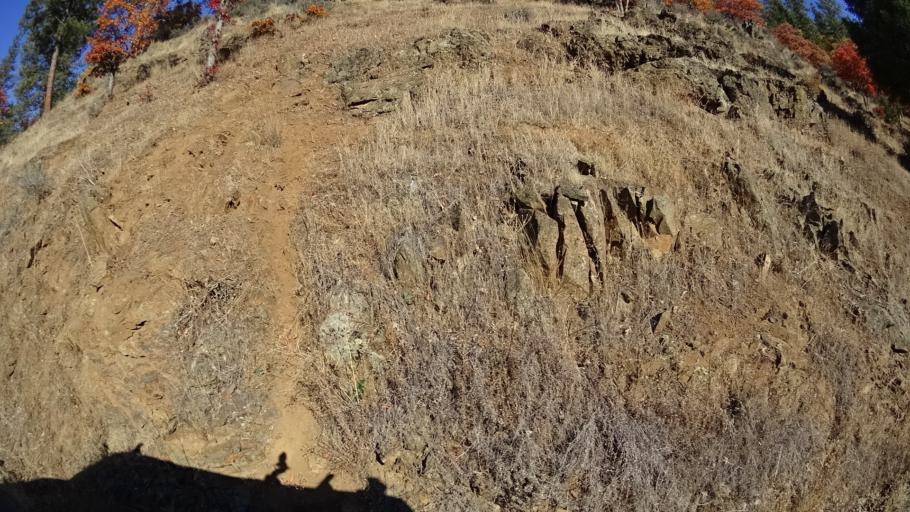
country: US
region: California
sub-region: Siskiyou County
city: Yreka
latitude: 41.6341
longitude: -122.9593
